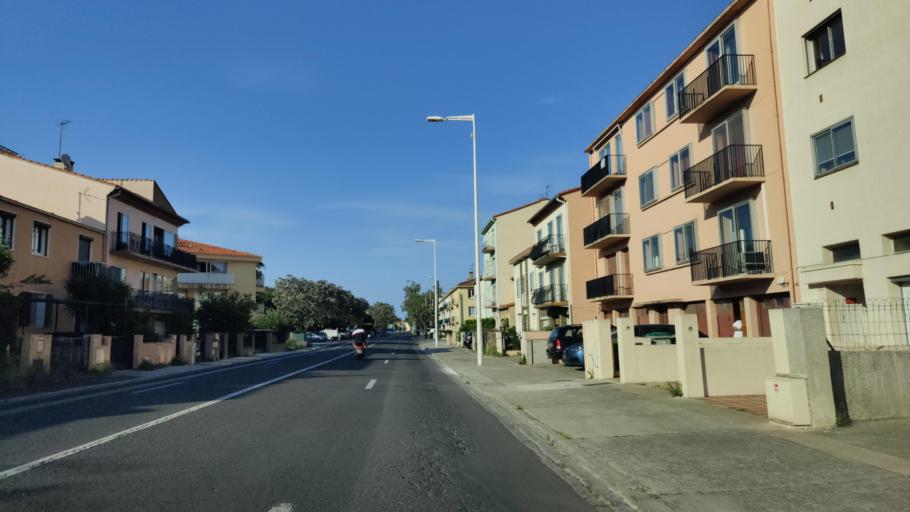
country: FR
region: Languedoc-Roussillon
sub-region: Departement des Pyrenees-Orientales
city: Perpignan
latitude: 42.7129
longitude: 2.8852
